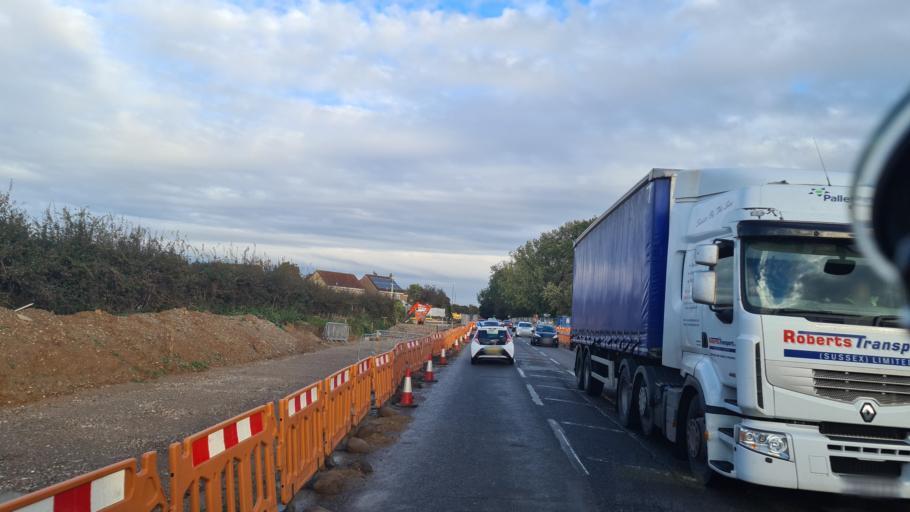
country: GB
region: England
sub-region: West Sussex
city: Littlehampton
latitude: 50.8211
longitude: -0.5393
